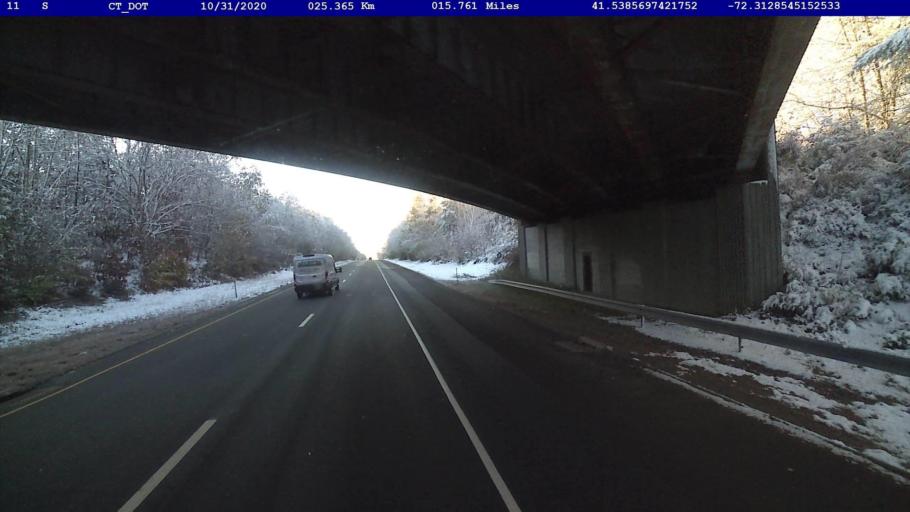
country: US
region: Connecticut
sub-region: New London County
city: Colchester
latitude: 41.5385
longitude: -72.3128
